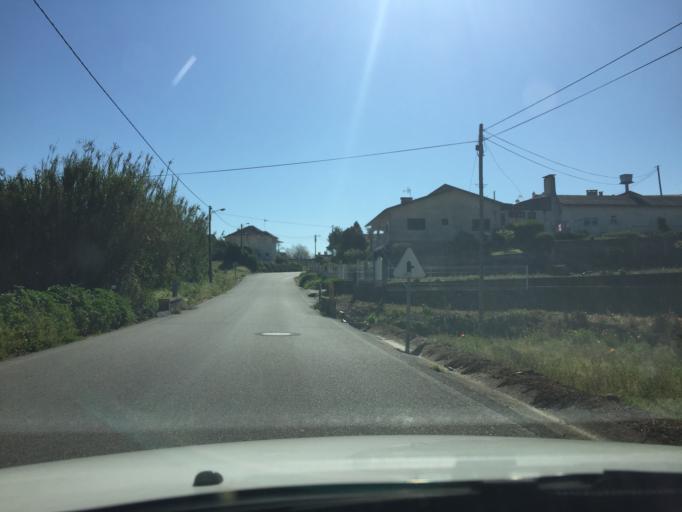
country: PT
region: Aveiro
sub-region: Oliveira do Bairro
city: Oliveira do Bairro
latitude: 40.4786
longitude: -8.5459
